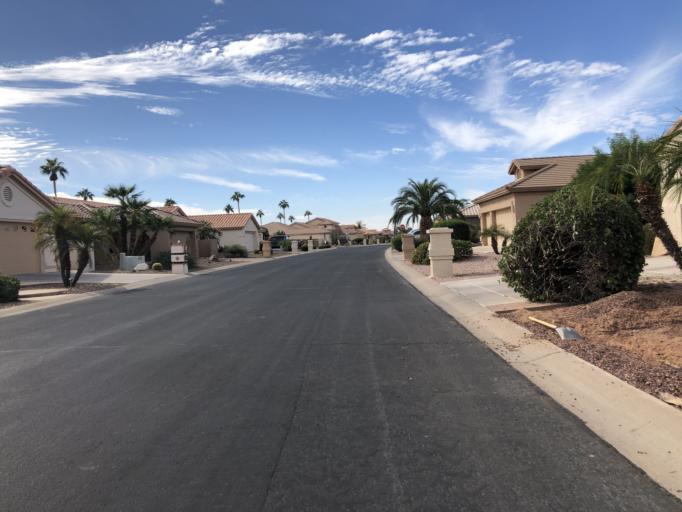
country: US
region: Arizona
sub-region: Maricopa County
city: Sun Lakes
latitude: 33.2280
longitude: -111.8826
